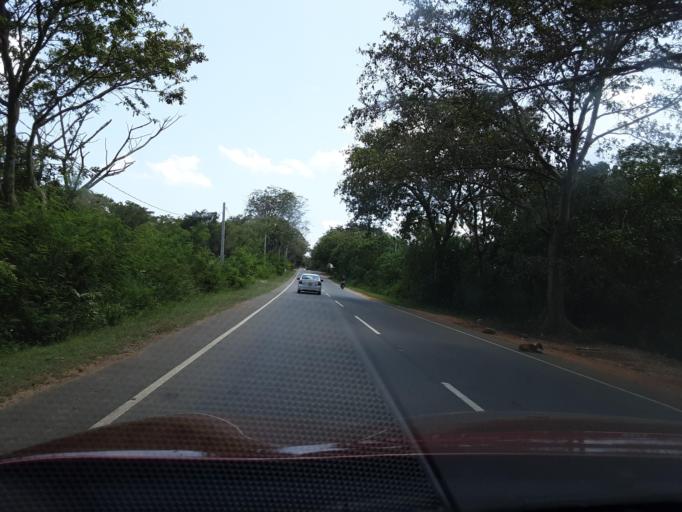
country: LK
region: Southern
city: Tangalla
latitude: 6.2295
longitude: 81.2240
